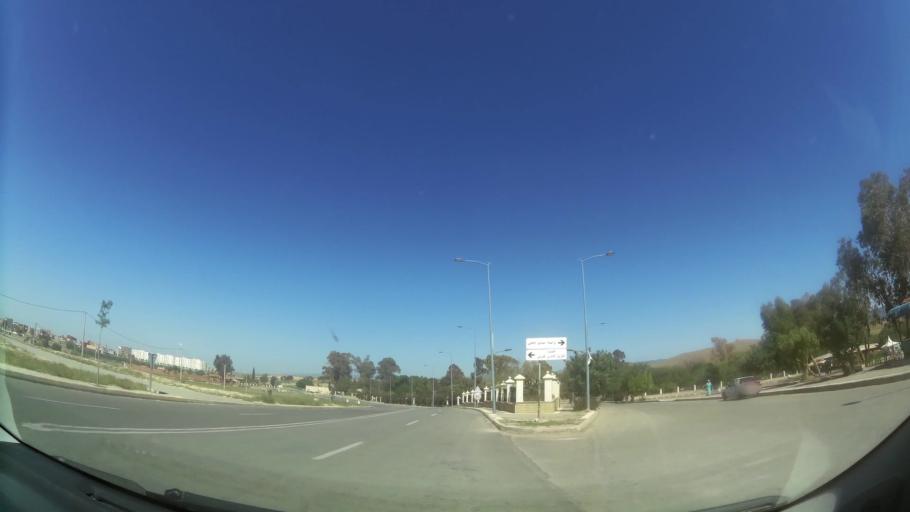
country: MA
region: Oriental
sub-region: Oujda-Angad
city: Oujda
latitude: 34.6664
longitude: -1.8658
